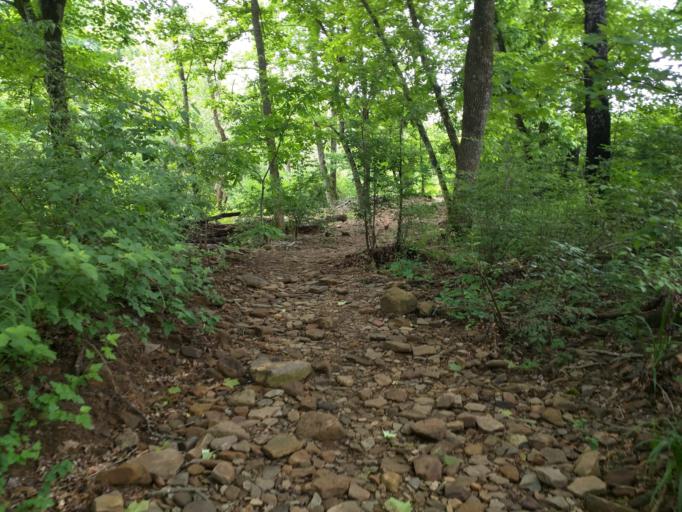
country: US
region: Arkansas
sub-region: Madison County
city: Huntsville
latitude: 35.8974
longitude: -93.5798
